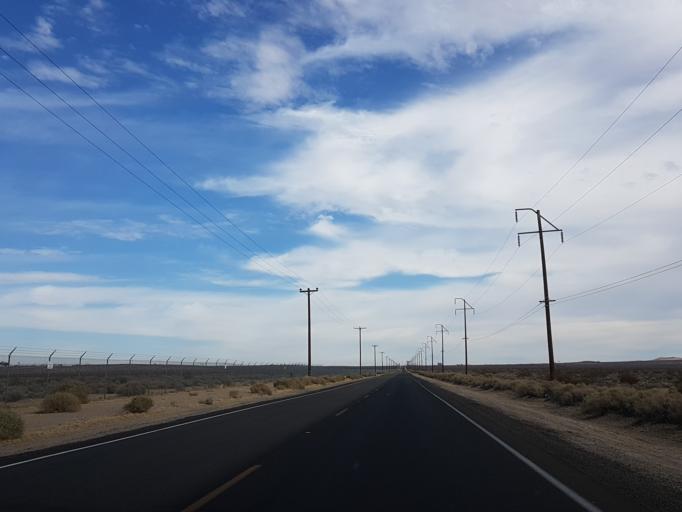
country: US
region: California
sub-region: Kern County
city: Ridgecrest
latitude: 35.6225
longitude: -117.6301
